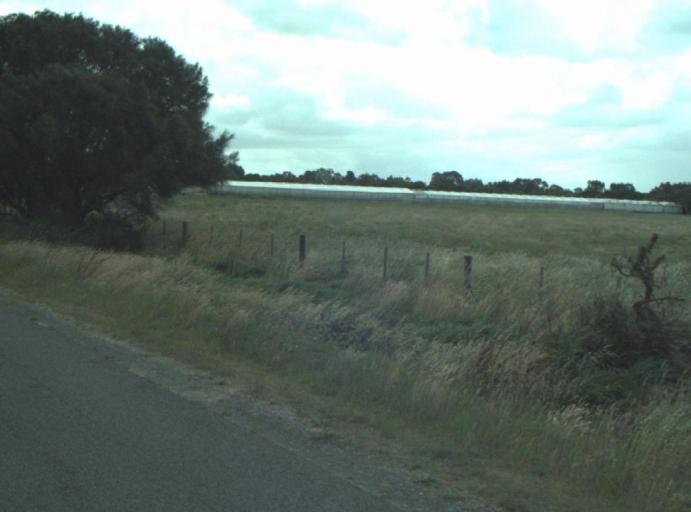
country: AU
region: Victoria
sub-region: Greater Geelong
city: Breakwater
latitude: -38.2204
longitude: 144.3448
